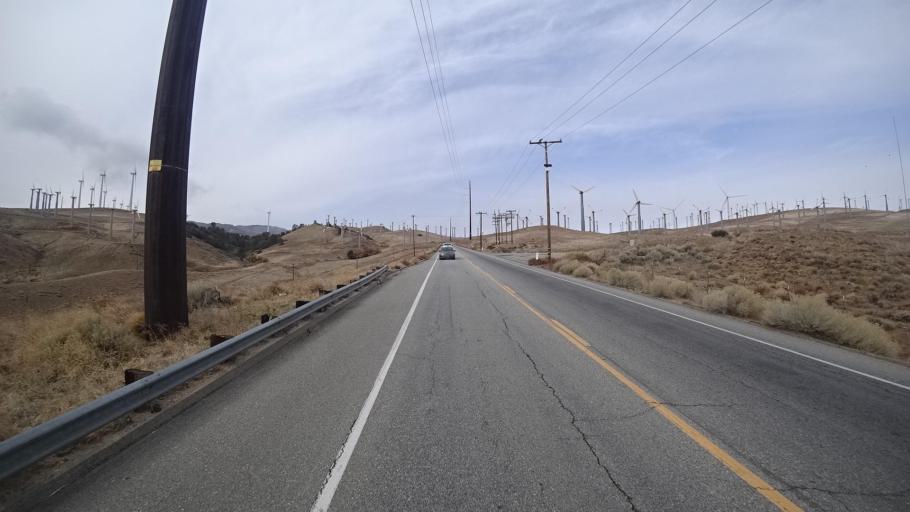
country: US
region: California
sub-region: Kern County
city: Tehachapi
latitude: 35.0566
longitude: -118.3802
